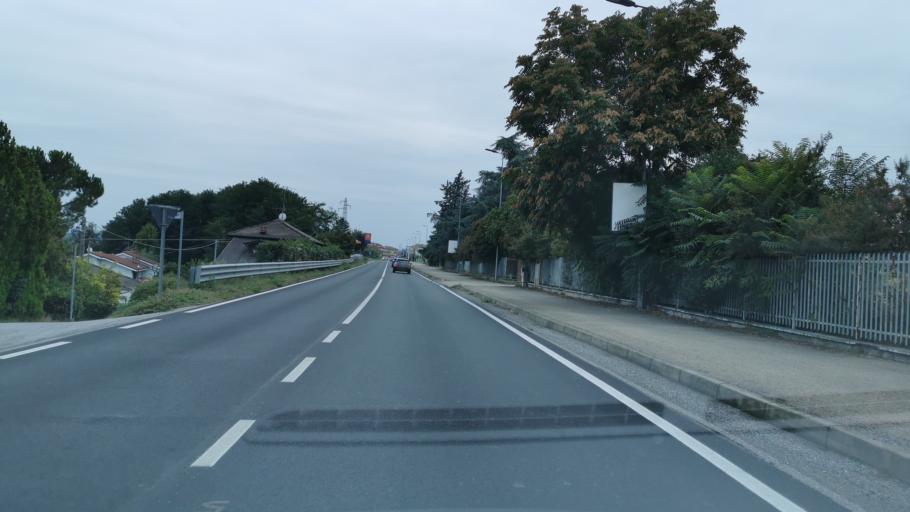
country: IT
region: Piedmont
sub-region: Provincia di Cuneo
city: Roreto
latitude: 44.6771
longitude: 7.8446
